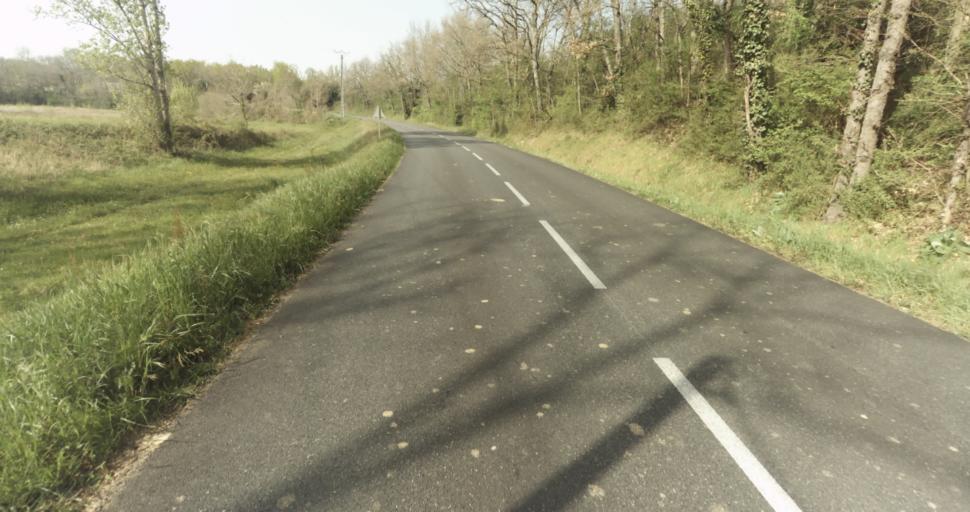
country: FR
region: Midi-Pyrenees
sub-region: Departement du Tarn-et-Garonne
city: Lafrancaise
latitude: 44.1522
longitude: 1.1824
